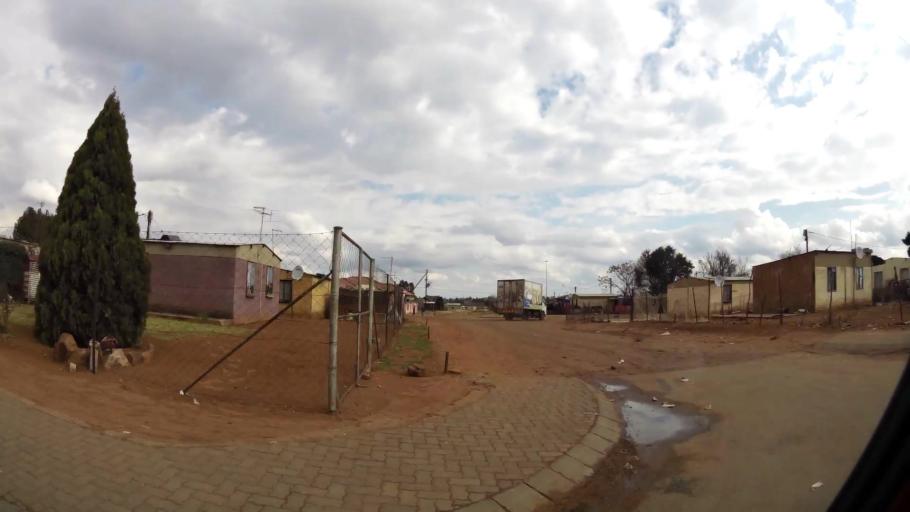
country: ZA
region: Gauteng
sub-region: Sedibeng District Municipality
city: Vanderbijlpark
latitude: -26.7021
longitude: 27.8040
